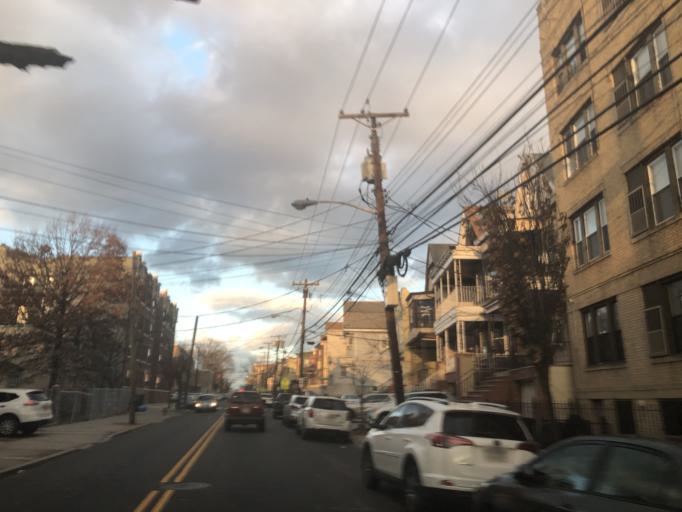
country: US
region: New Jersey
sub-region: Hudson County
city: Jersey City
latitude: 40.7082
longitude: -74.0855
